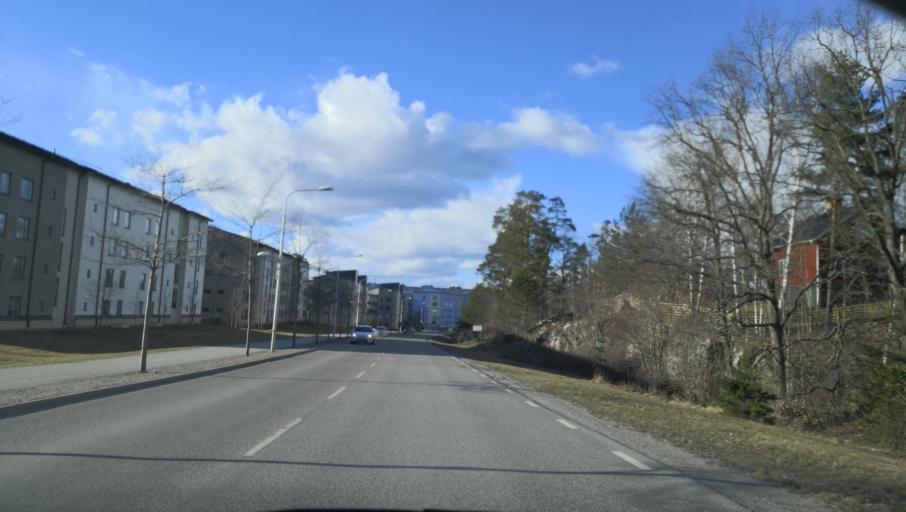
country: SE
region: Stockholm
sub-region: Varmdo Kommun
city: Gustavsberg
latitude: 59.3173
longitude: 18.3904
